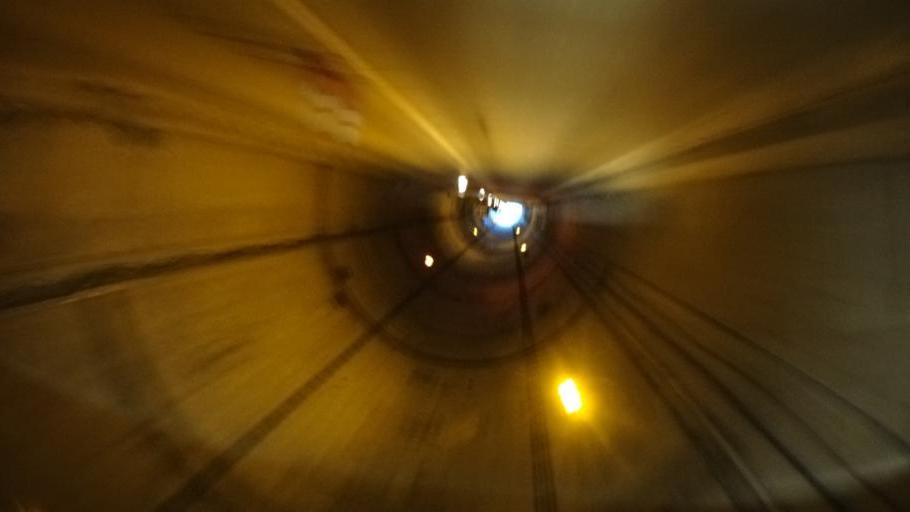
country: JP
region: Fukui
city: Maruoka
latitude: 36.1221
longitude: 136.3194
